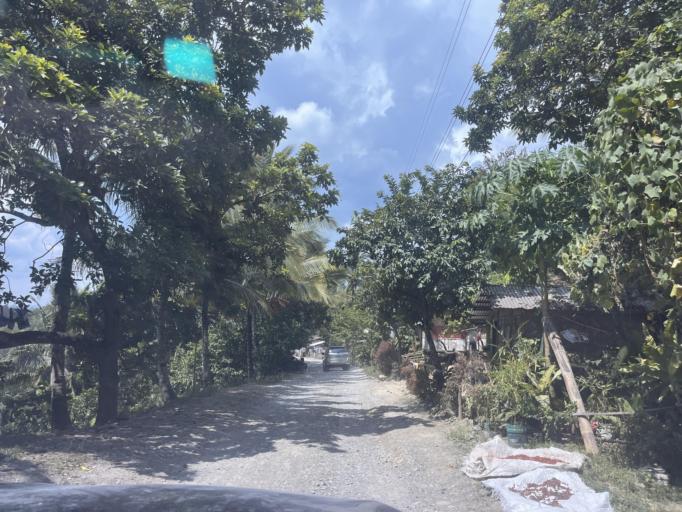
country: PH
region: Davao
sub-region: Province of Davao del Sur
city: Tamugan
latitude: 7.2884
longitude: 125.3389
